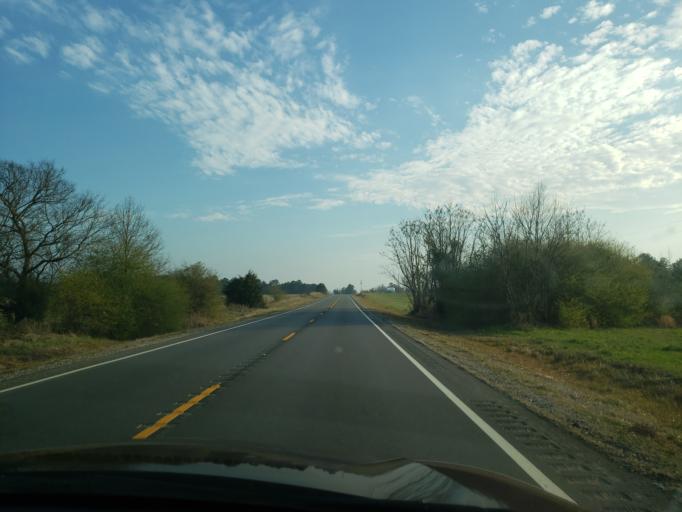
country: US
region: Alabama
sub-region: Hale County
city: Moundville
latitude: 32.8726
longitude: -87.6112
